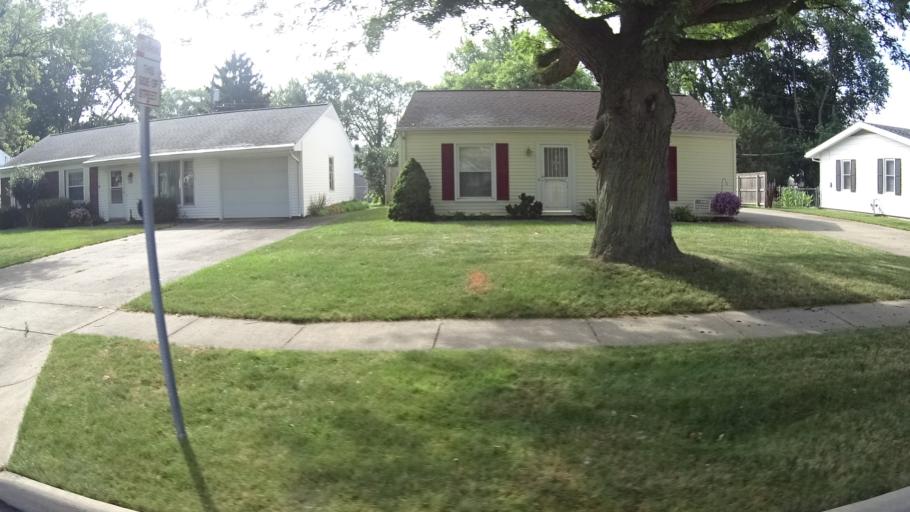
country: US
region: Ohio
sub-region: Erie County
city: Sandusky
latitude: 41.4342
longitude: -82.6764
